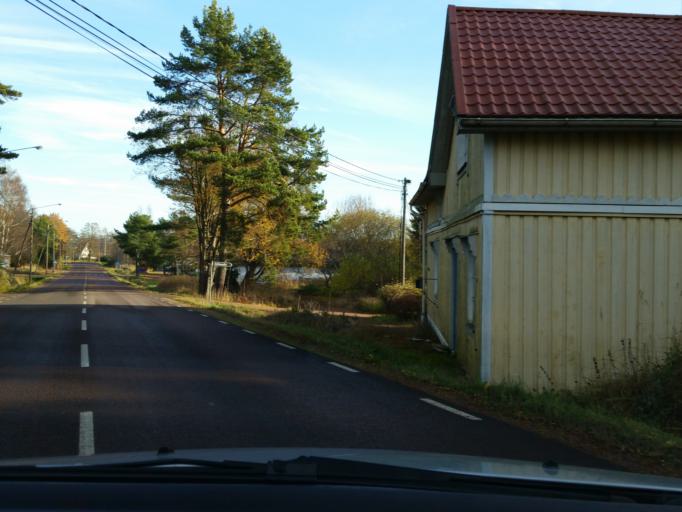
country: AX
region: Alands landsbygd
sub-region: Finstroem
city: Finstroem
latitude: 60.3079
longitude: 19.9635
